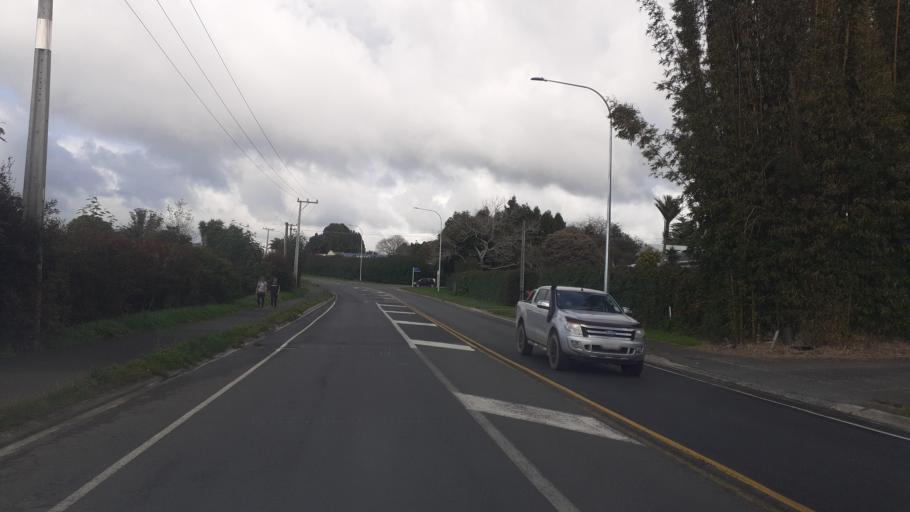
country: NZ
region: Northland
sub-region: Far North District
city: Kerikeri
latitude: -35.2404
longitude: 173.9379
